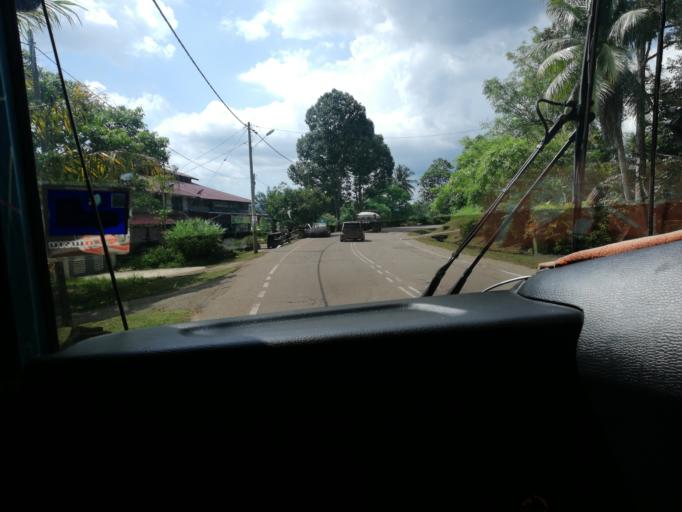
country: MY
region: Penang
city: Nibong Tebal
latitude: 5.2168
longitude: 100.6102
